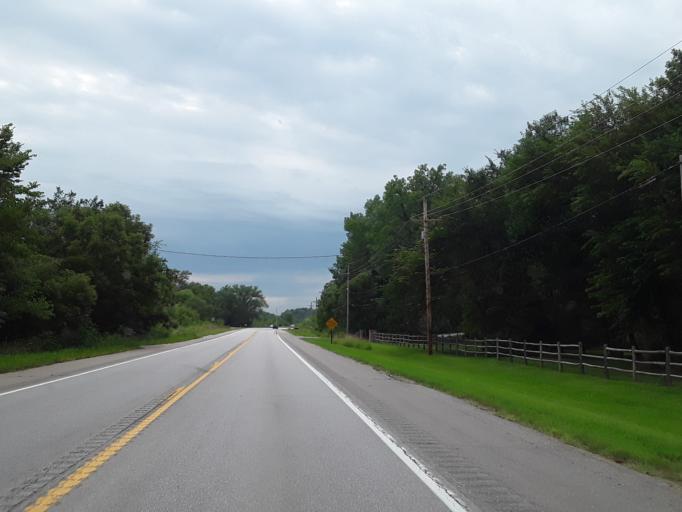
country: US
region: Nebraska
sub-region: Saunders County
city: Yutan
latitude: 41.2338
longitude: -96.3483
